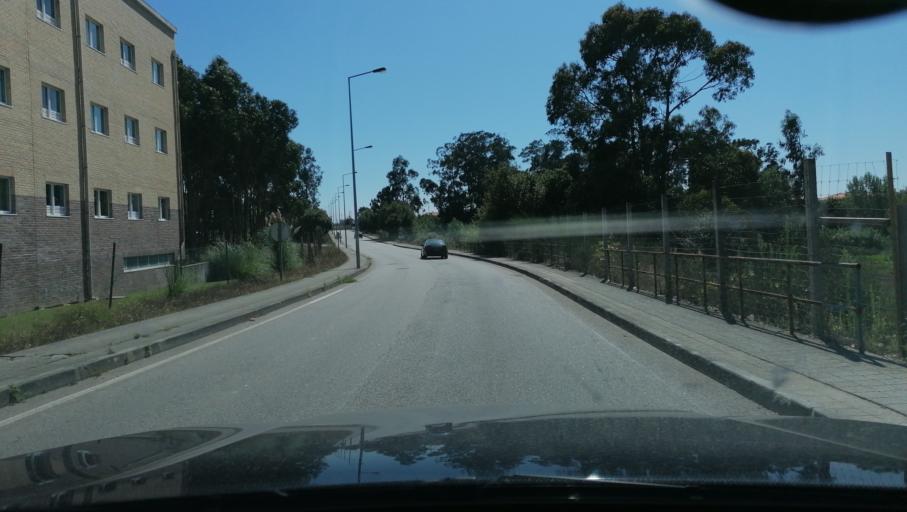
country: PT
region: Porto
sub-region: Vila Nova de Gaia
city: Vila Nova da Telha
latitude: 41.0770
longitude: -8.6415
